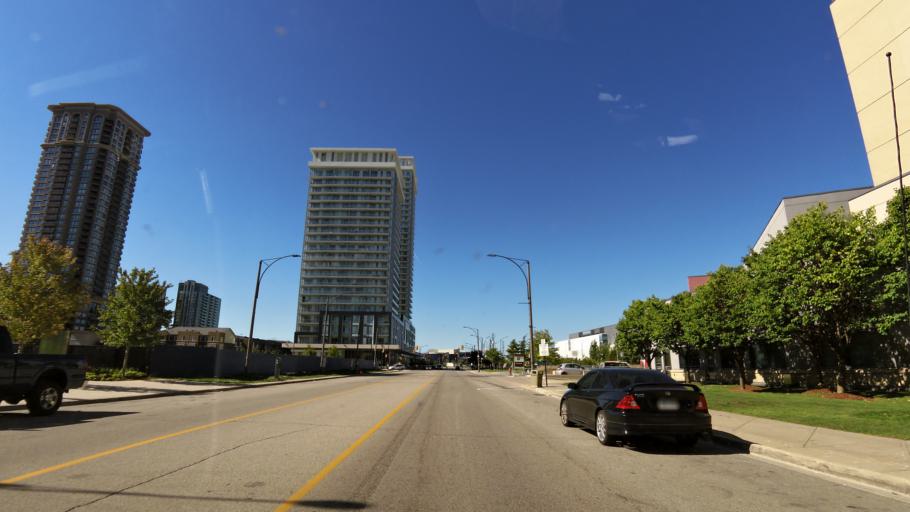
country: CA
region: Ontario
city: Mississauga
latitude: 43.5889
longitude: -79.6462
